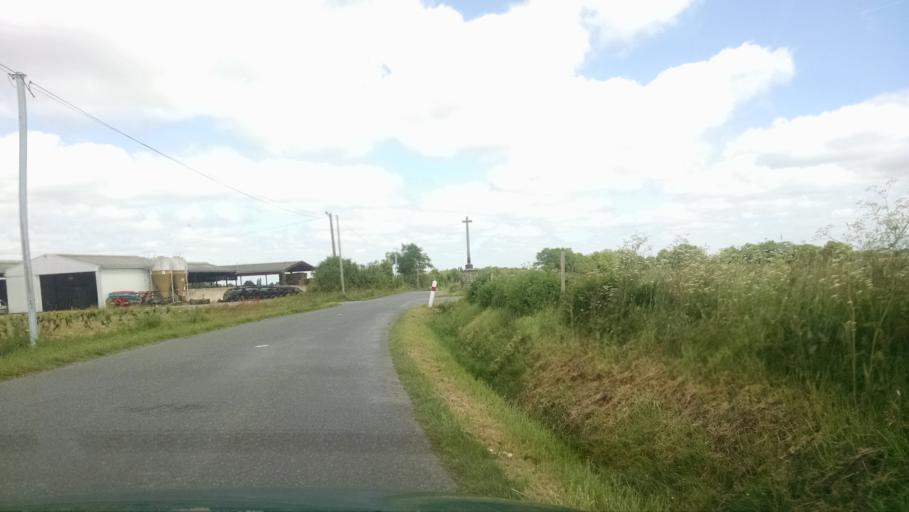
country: FR
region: Pays de la Loire
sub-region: Departement de la Loire-Atlantique
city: Saint-Hilaire-de-Clisson
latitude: 47.0729
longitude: -1.3112
